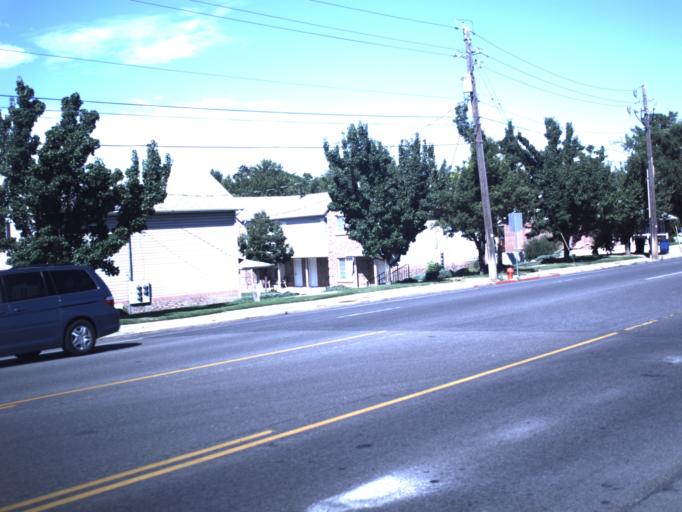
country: US
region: Utah
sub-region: Davis County
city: Kaysville
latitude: 41.0325
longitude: -111.9374
